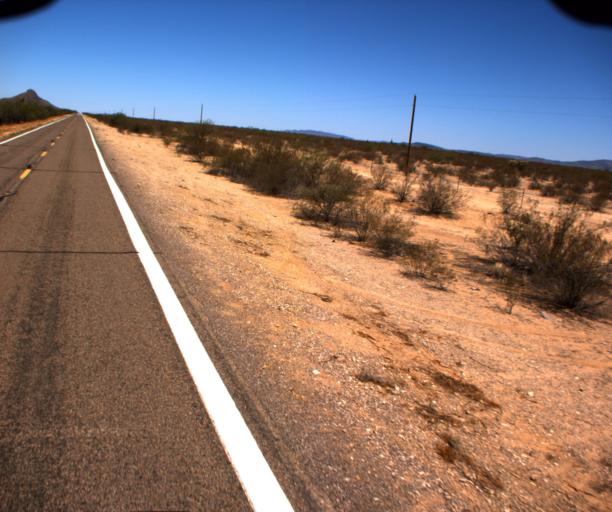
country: US
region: Arizona
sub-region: Pima County
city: Ajo
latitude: 32.1989
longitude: -112.4841
